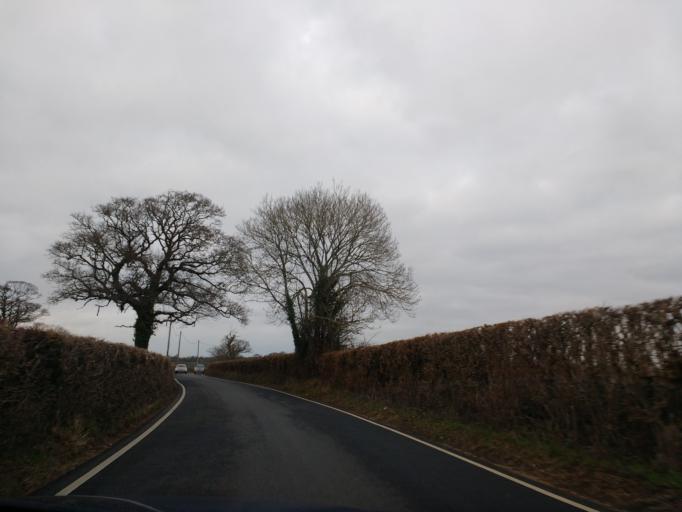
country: GB
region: England
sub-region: Isle of Wight
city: Shalfleet
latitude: 50.7067
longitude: -1.4052
